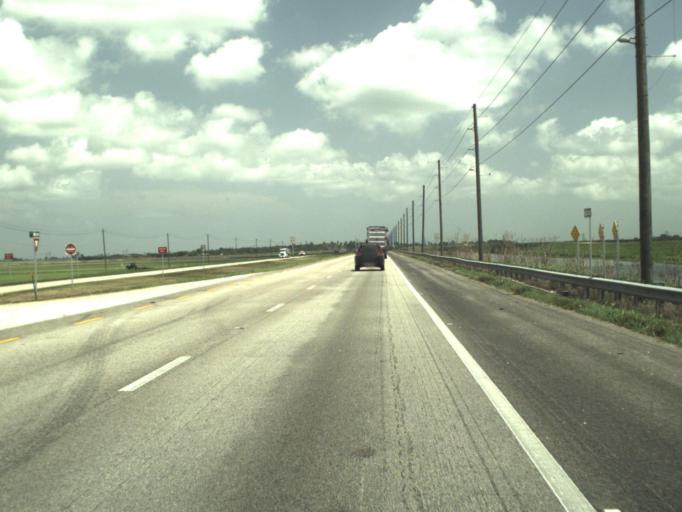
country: US
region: Florida
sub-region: Palm Beach County
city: South Bay
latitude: 26.6313
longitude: -80.7120
